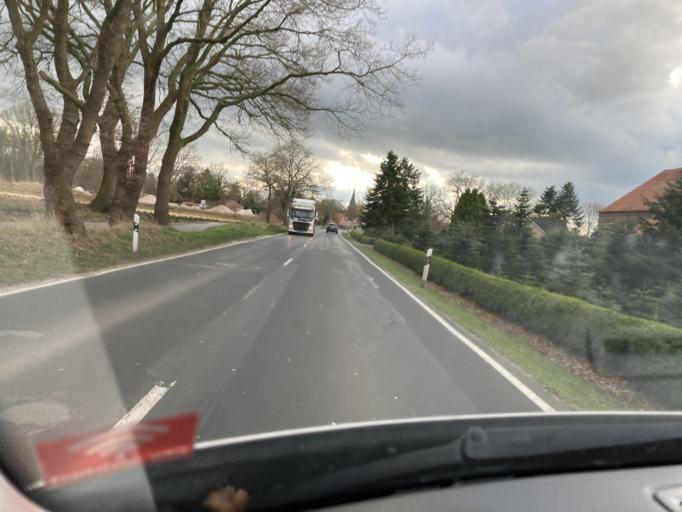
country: DE
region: Lower Saxony
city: Schwerinsdorf
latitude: 53.3113
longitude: 7.7541
